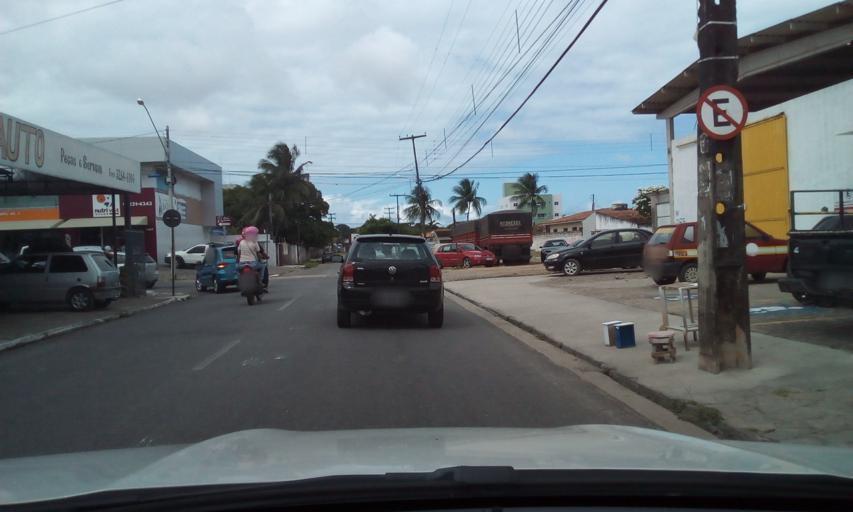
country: BR
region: Paraiba
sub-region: Joao Pessoa
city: Joao Pessoa
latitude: -7.1595
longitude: -34.8716
